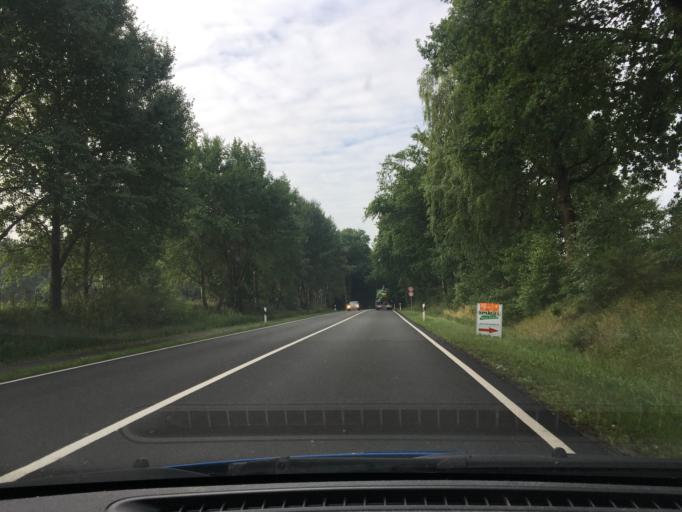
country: DE
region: Lower Saxony
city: Wenzendorf
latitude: 53.3664
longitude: 9.8056
